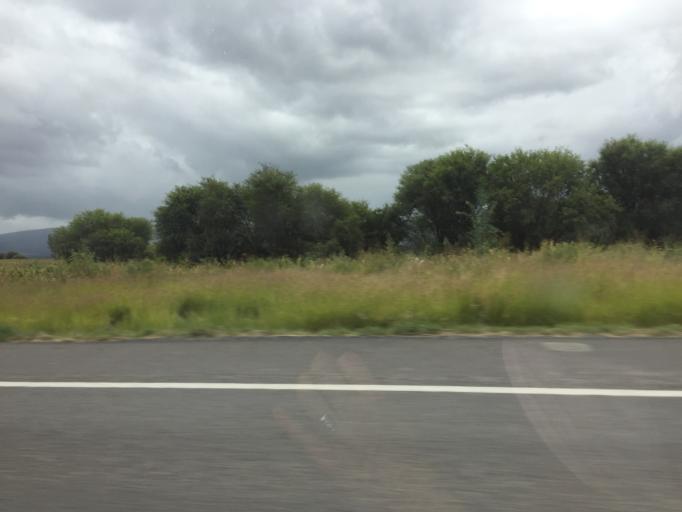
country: MX
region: Jalisco
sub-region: Zapotlanejo
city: La Mezquitera
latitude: 20.5628
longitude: -103.0742
